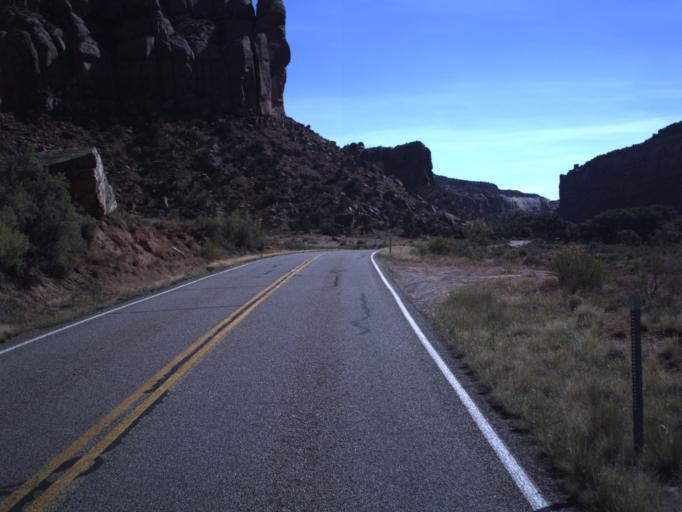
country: US
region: Utah
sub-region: San Juan County
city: Monticello
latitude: 38.0444
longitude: -109.5516
